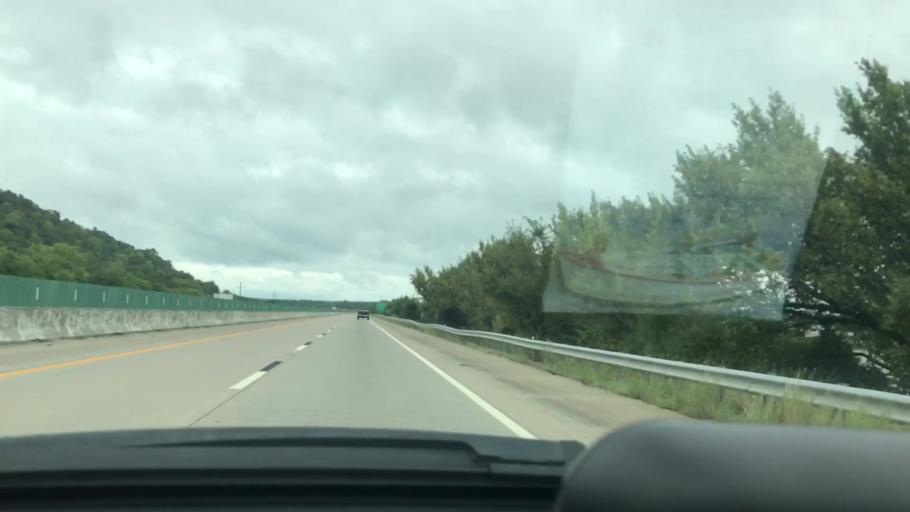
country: US
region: Oklahoma
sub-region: McIntosh County
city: Eufaula
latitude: 35.1203
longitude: -95.6826
